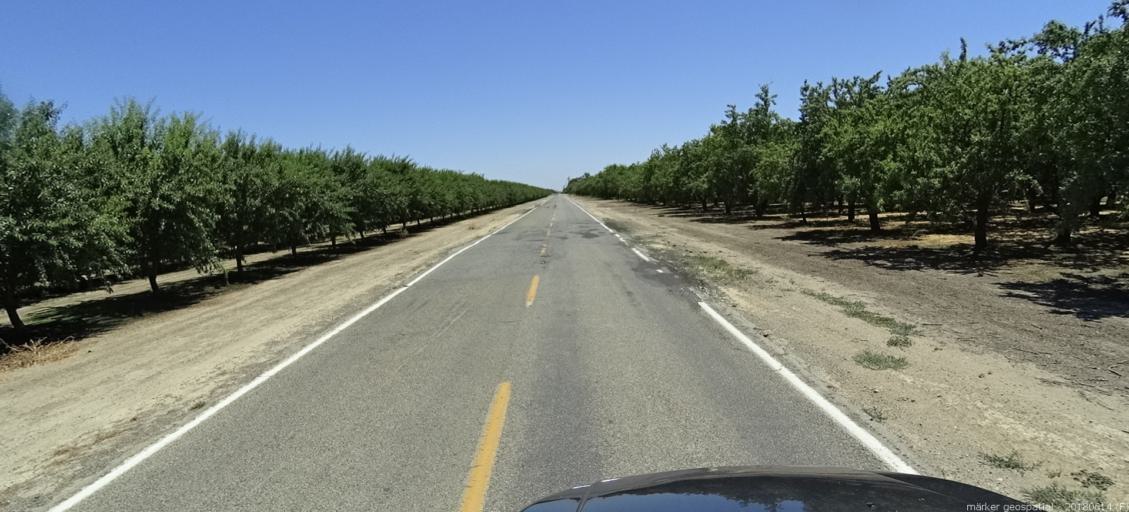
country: US
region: California
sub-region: Madera County
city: Fairmead
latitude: 37.0183
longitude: -120.2473
